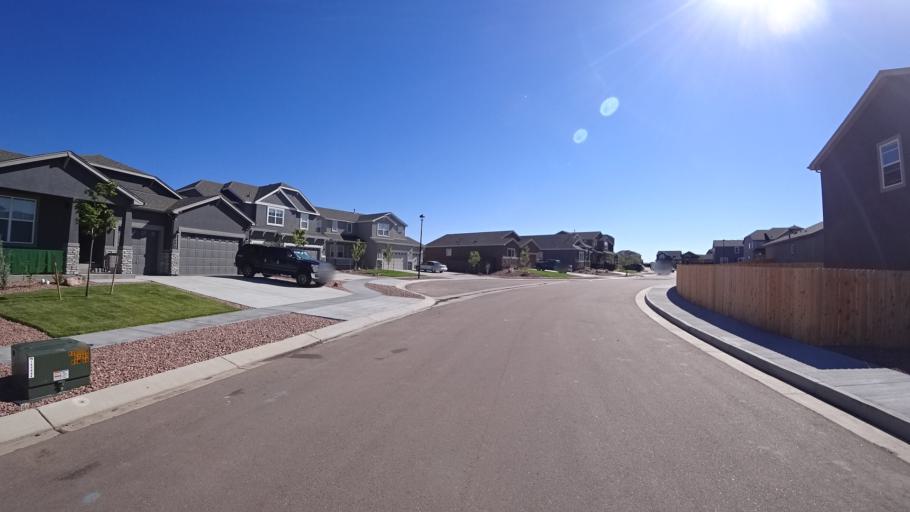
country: US
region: Colorado
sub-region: El Paso County
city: Black Forest
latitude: 38.9511
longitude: -104.6761
